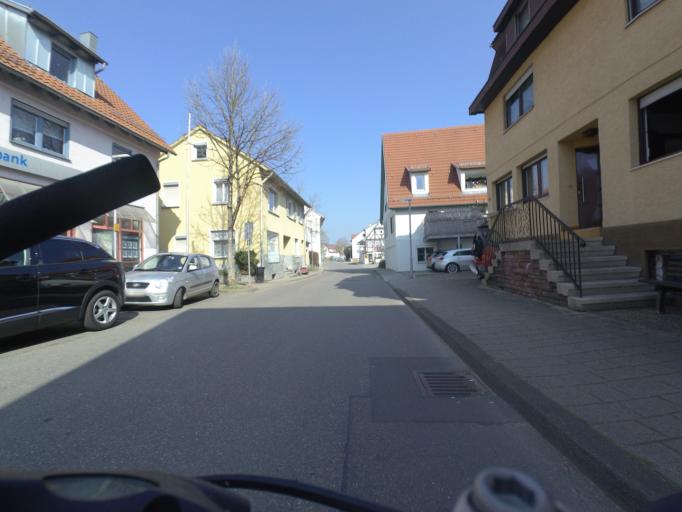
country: DE
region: Baden-Wuerttemberg
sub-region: Regierungsbezirk Stuttgart
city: Unterensingen
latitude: 48.6565
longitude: 9.3560
